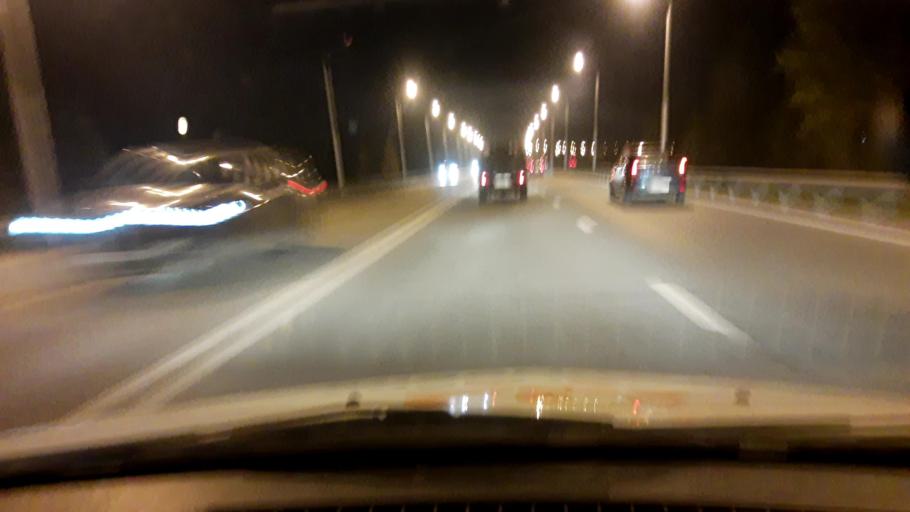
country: RU
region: Bashkortostan
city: Iglino
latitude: 54.8008
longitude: 56.1963
